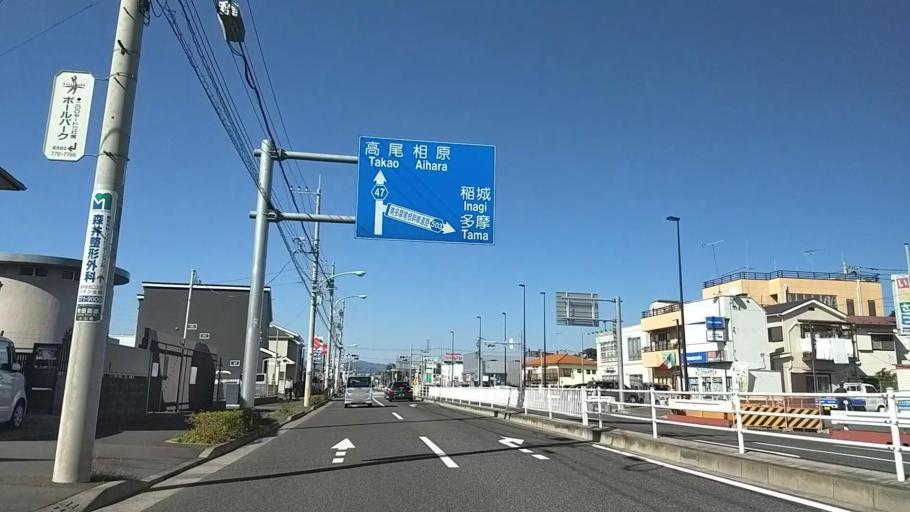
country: JP
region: Tokyo
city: Hachioji
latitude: 35.5949
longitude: 139.3742
